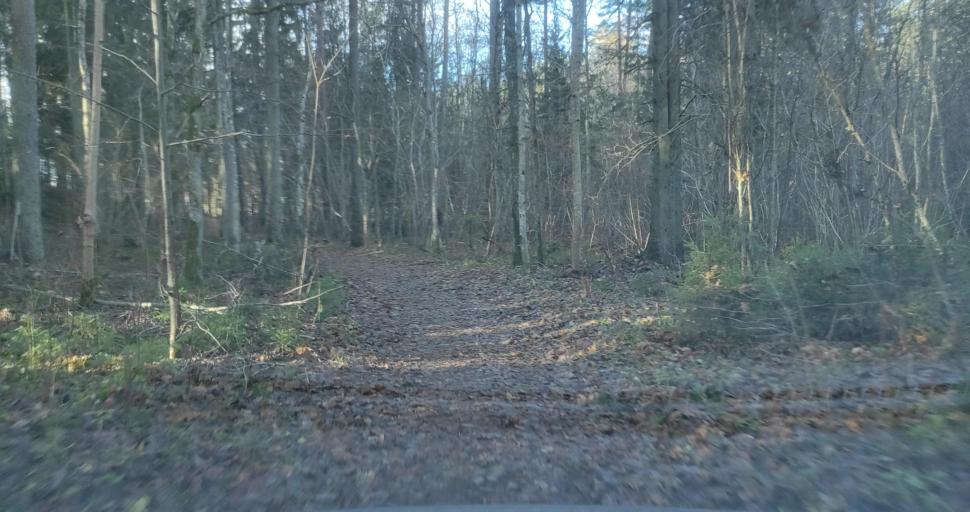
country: LV
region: Kuldigas Rajons
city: Kuldiga
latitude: 56.9611
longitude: 21.9306
